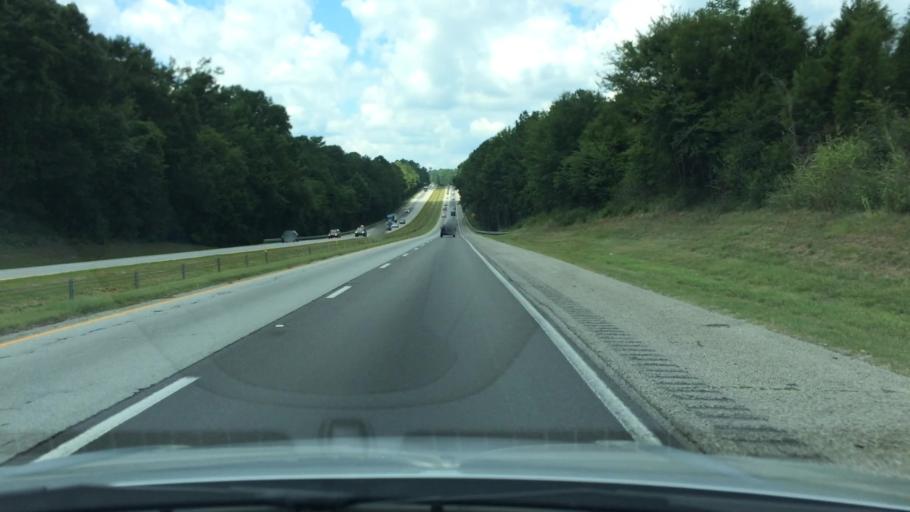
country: US
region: South Carolina
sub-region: Newberry County
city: Prosperity
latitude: 34.2298
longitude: -81.4360
